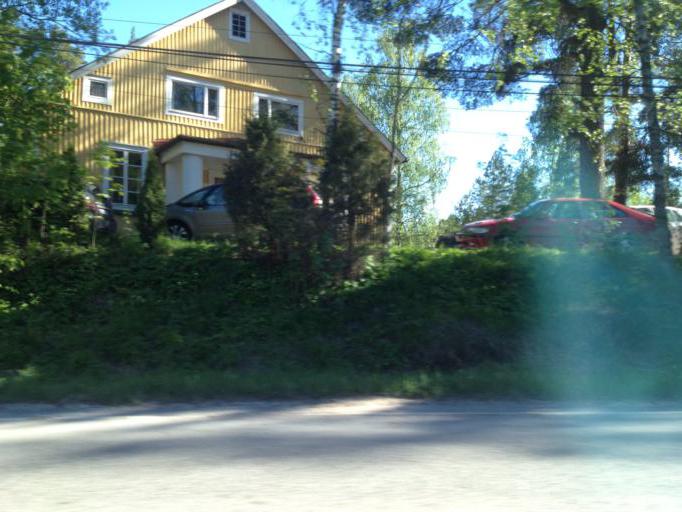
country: FI
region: Uusimaa
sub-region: Helsinki
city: Espoo
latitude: 60.2445
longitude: 24.5718
